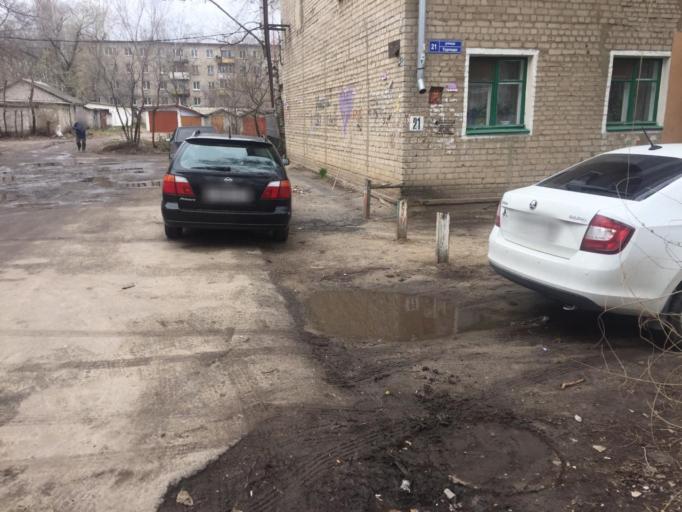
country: RU
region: Voronezj
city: Voronezh
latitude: 51.6762
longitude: 39.1526
